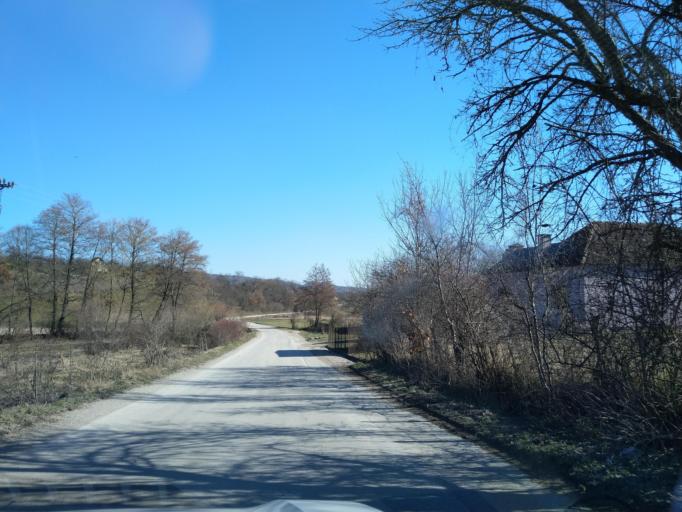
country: RS
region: Central Serbia
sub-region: Zlatiborski Okrug
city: Kosjeric
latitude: 43.9388
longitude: 19.8765
